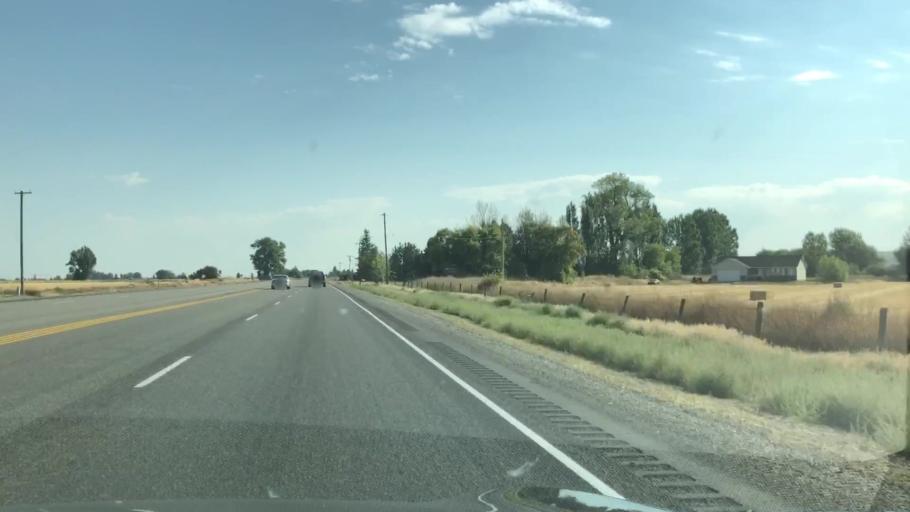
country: US
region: Idaho
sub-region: Bonneville County
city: Iona
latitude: 43.5535
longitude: -111.9433
